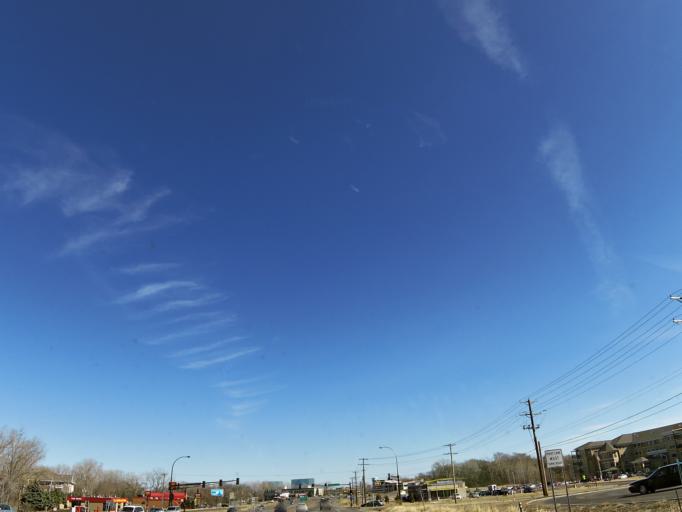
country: US
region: Minnesota
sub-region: Hennepin County
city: Plymouth
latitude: 44.9892
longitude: -93.4257
